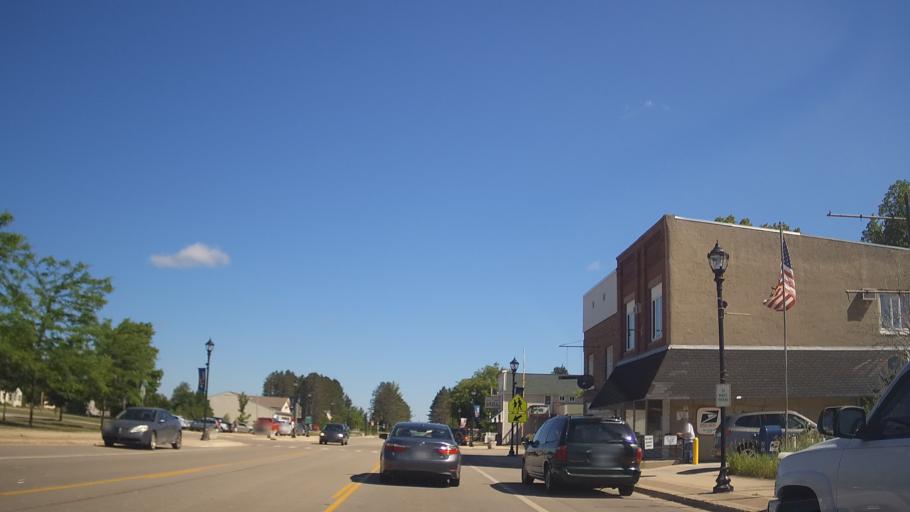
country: US
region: Michigan
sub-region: Cheboygan County
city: Indian River
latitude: 45.5528
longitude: -84.7844
